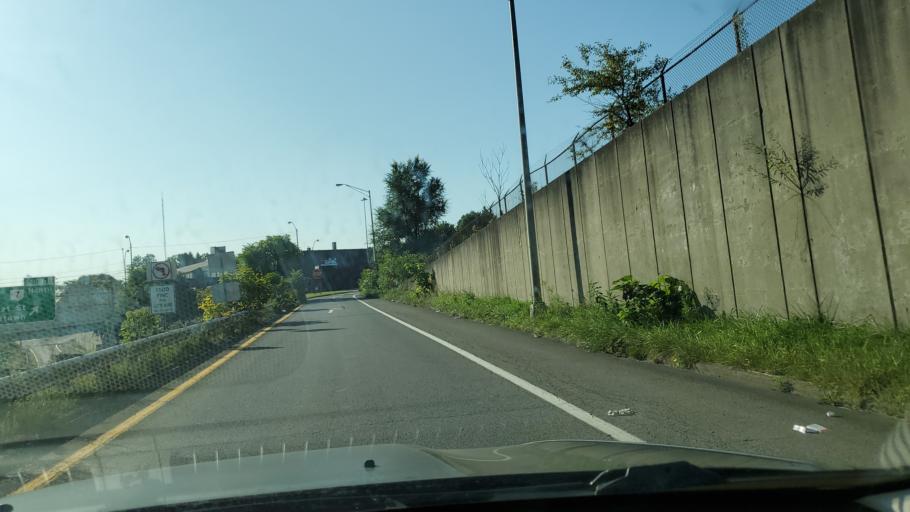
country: US
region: Ohio
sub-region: Mahoning County
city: Youngstown
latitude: 41.0931
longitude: -80.6563
